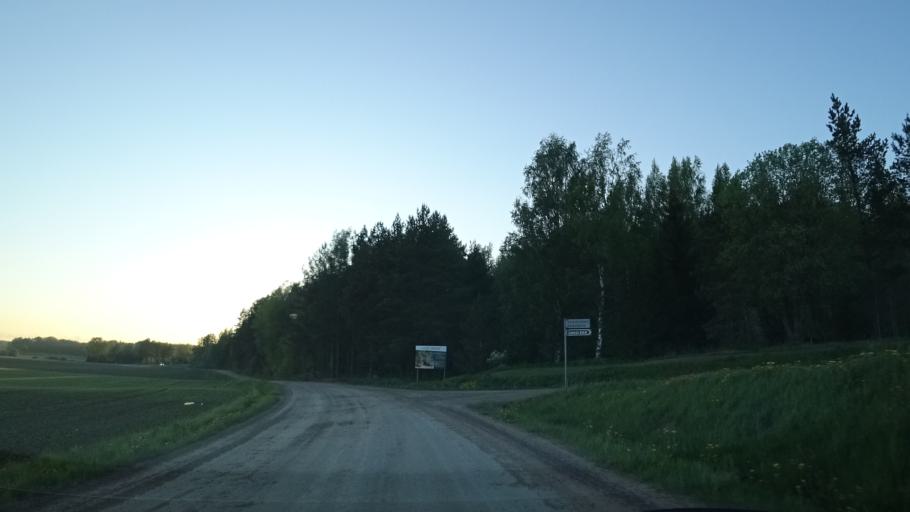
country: FI
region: Uusimaa
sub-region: Helsinki
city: Siuntio
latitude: 60.0791
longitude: 24.1920
